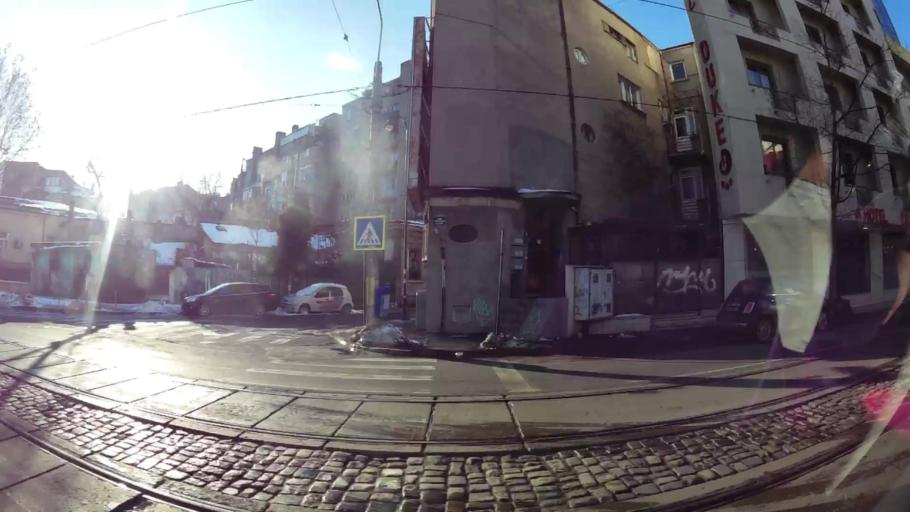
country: RO
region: Bucuresti
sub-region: Municipiul Bucuresti
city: Bucharest
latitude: 44.4384
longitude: 26.1092
